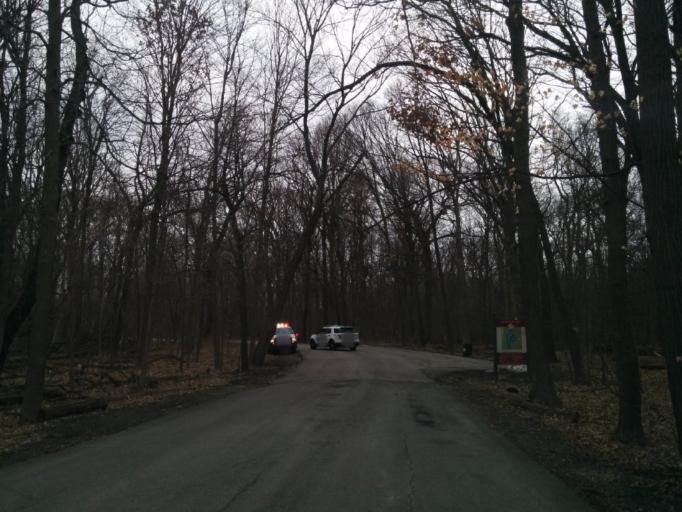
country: US
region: Illinois
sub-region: Cook County
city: Prospect Heights
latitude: 42.0880
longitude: -87.8849
